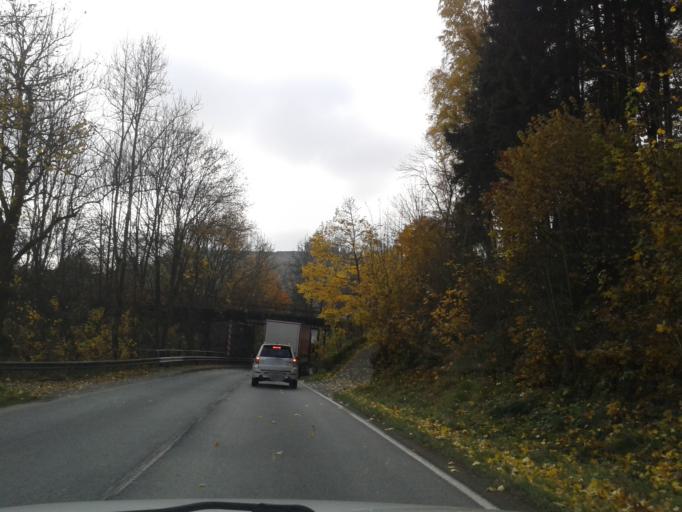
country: DE
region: North Rhine-Westphalia
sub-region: Regierungsbezirk Arnsberg
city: Bad Berleburg
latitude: 51.0316
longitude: 8.3851
